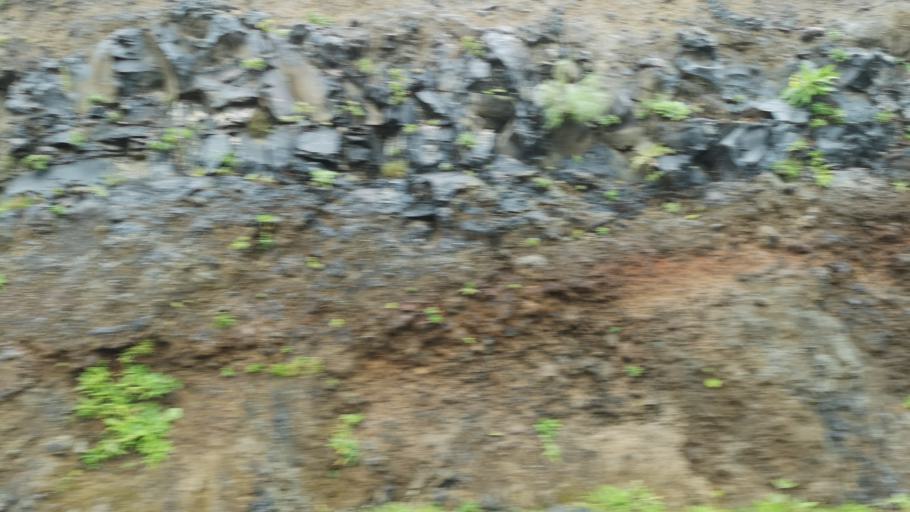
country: ES
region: Canary Islands
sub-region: Provincia de Santa Cruz de Tenerife
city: Alajero
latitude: 28.0953
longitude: -17.1906
